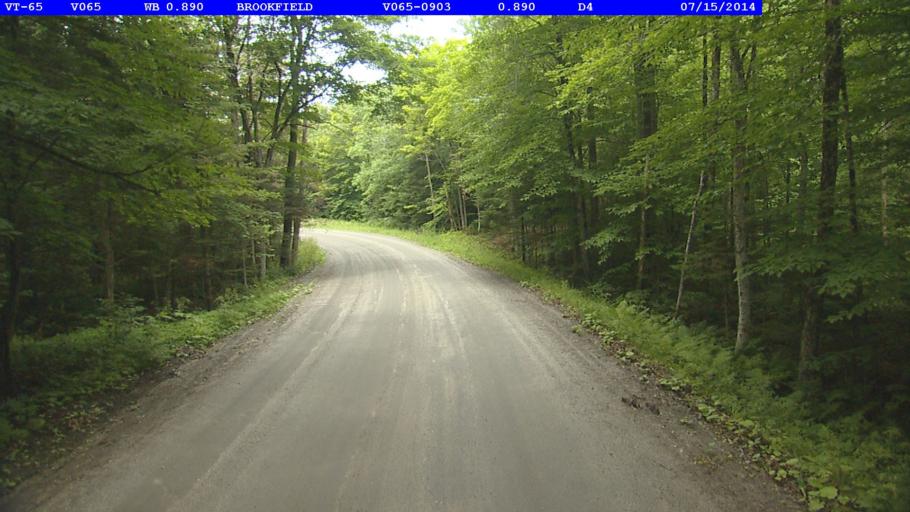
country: US
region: Vermont
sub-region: Washington County
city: Northfield
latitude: 44.0574
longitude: -72.6273
